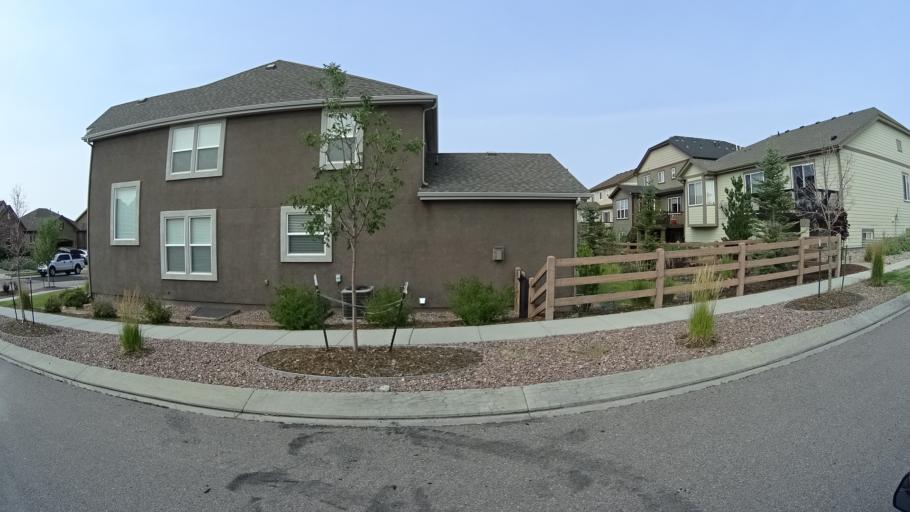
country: US
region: Colorado
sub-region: El Paso County
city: Black Forest
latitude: 38.9663
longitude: -104.7242
